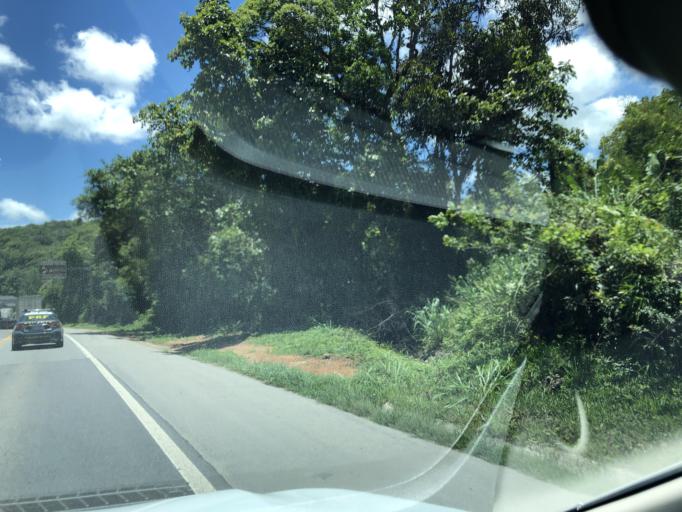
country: BR
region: Santa Catarina
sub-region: Joinville
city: Joinville
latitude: -26.4328
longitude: -48.8024
